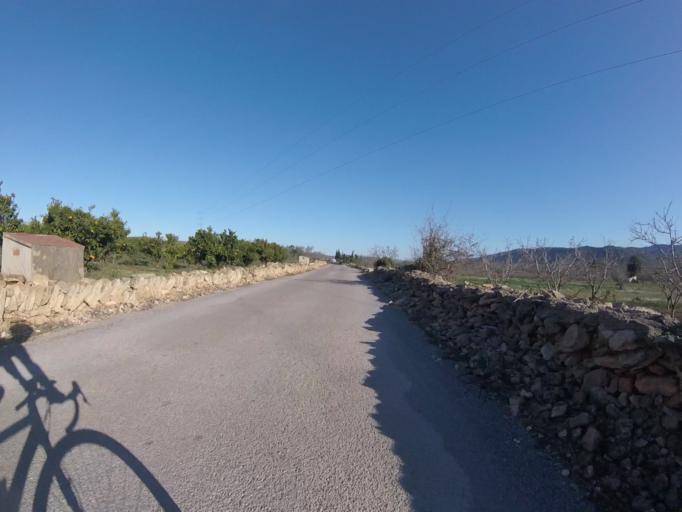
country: ES
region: Valencia
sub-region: Provincia de Castello
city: Alcala de Xivert
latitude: 40.2898
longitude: 0.2160
